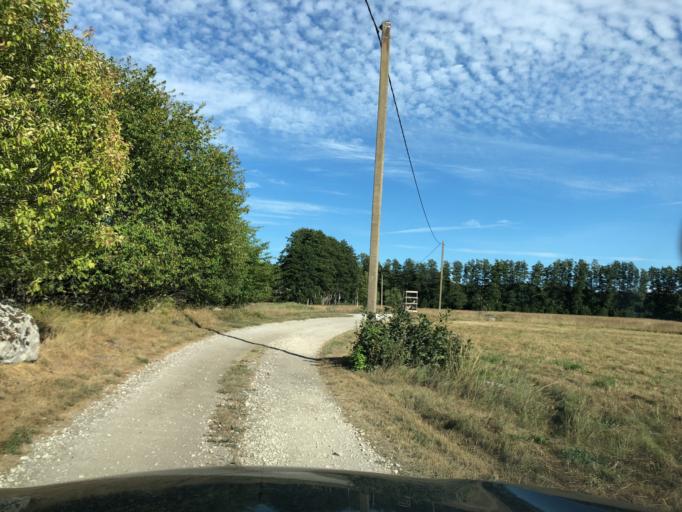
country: EE
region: Laeaene
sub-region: Haapsalu linn
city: Haapsalu
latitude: 58.7818
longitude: 23.4800
